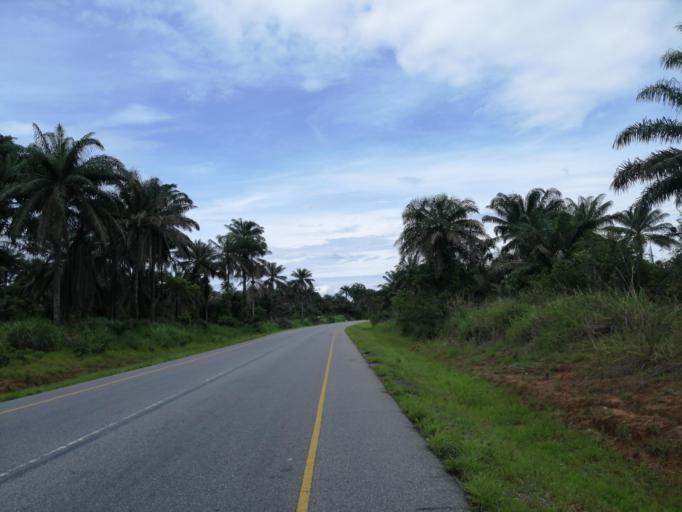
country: SL
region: Northern Province
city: Port Loko
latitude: 8.7603
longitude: -12.9100
